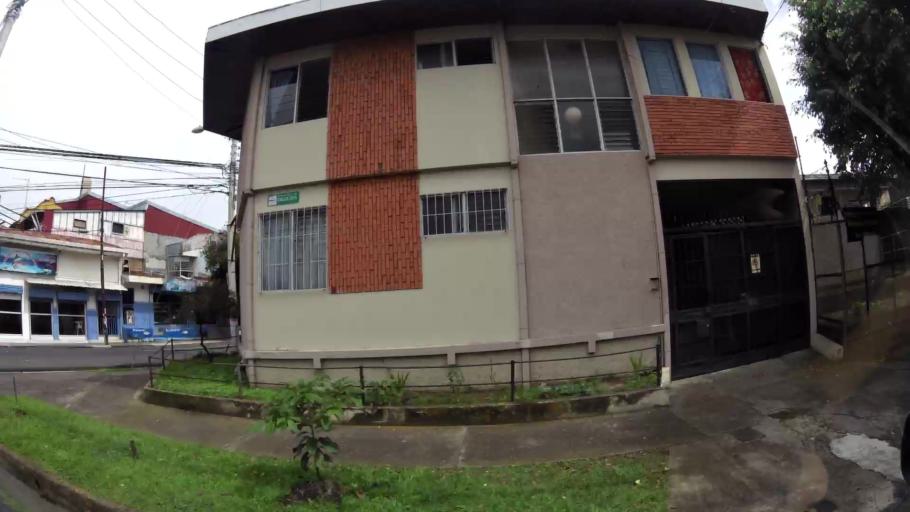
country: CR
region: San Jose
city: San Pedro
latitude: 9.9289
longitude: -84.0670
